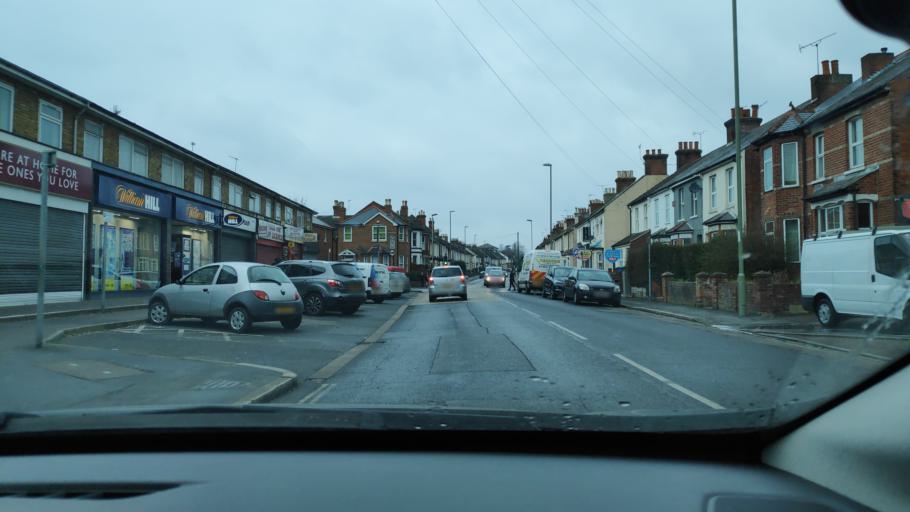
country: GB
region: England
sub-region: Hampshire
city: Aldershot
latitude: 51.2420
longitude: -0.7439
